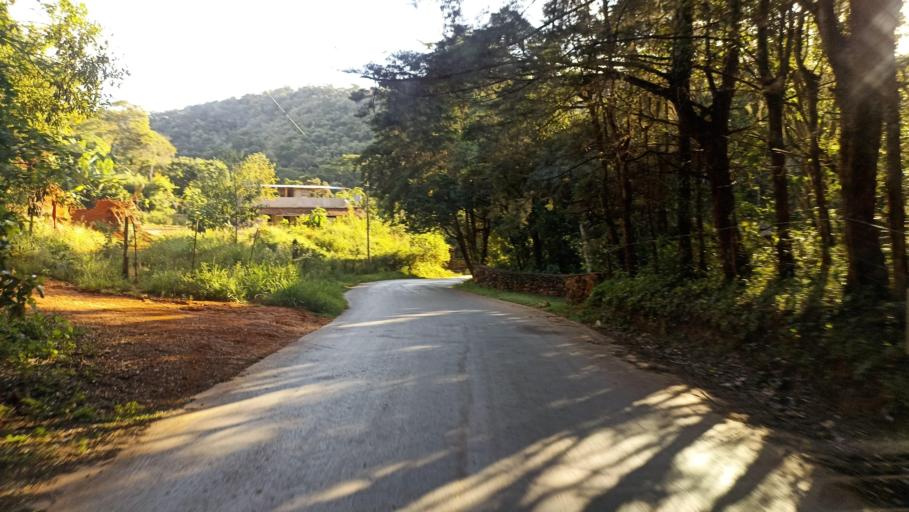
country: BR
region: Minas Gerais
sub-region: Ouro Preto
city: Ouro Preto
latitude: -20.3125
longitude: -43.6136
